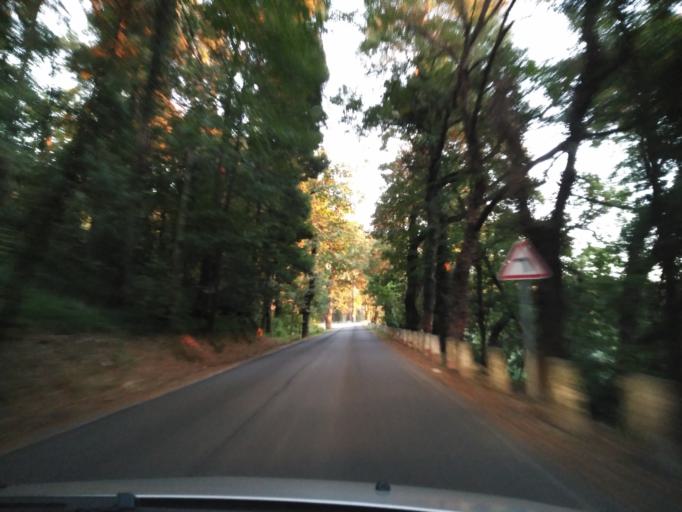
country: PT
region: Braga
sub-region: Braga
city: Adaufe
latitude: 41.5529
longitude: -8.3799
